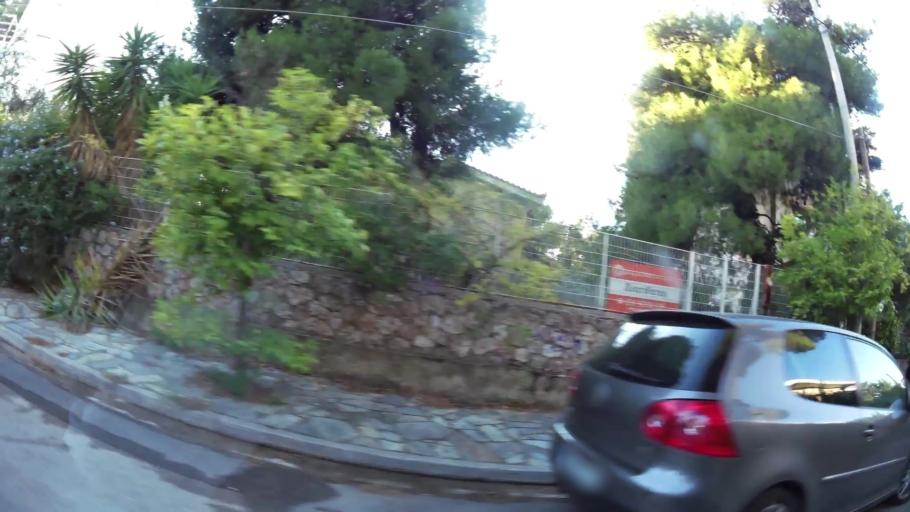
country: GR
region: Attica
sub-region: Nomarchia Athinas
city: Nea Erythraia
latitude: 38.0900
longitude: 23.8251
